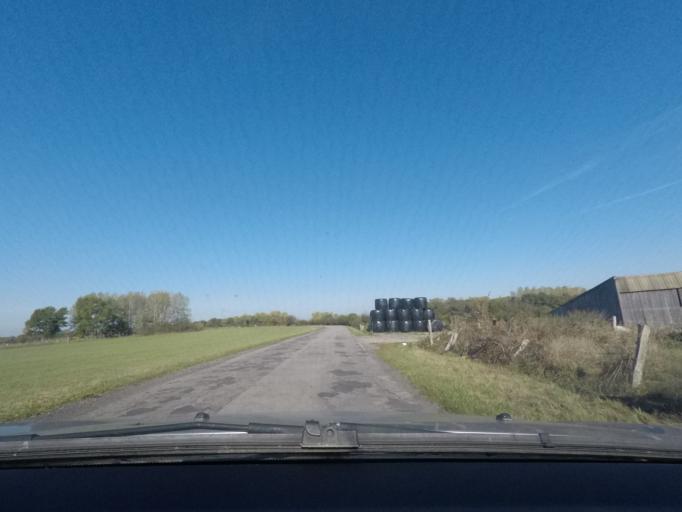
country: BE
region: Wallonia
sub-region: Province du Luxembourg
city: Etalle
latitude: 49.6866
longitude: 5.5842
